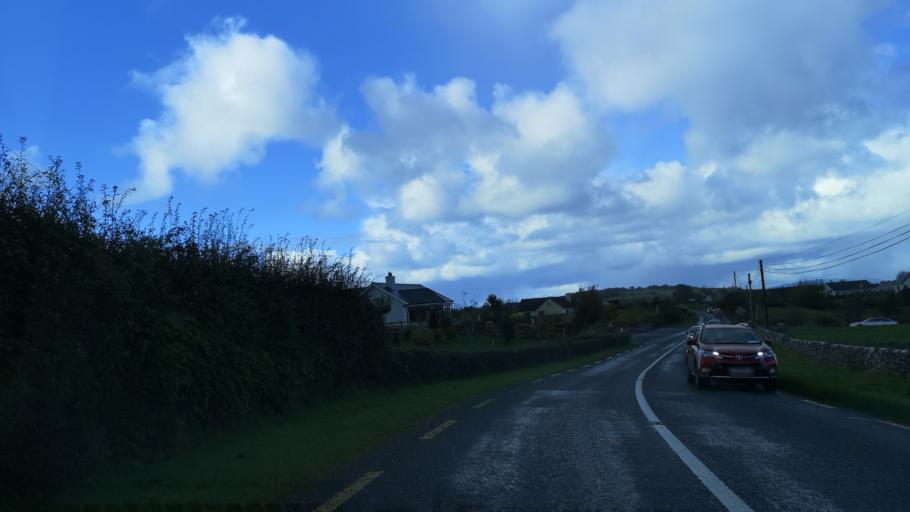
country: IE
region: Connaught
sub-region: Maigh Eo
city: Westport
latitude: 53.7791
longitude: -9.4324
